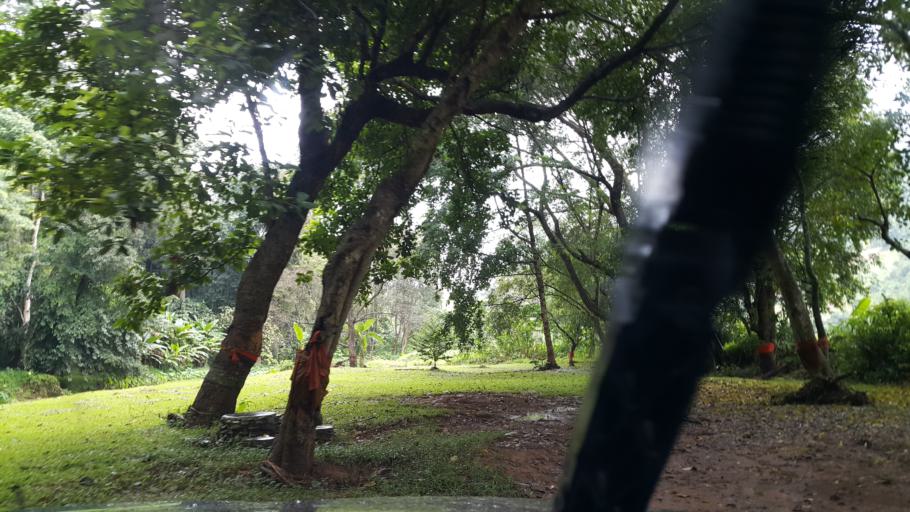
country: TH
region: Phayao
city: Chiang Kham
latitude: 19.5007
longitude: 100.4507
